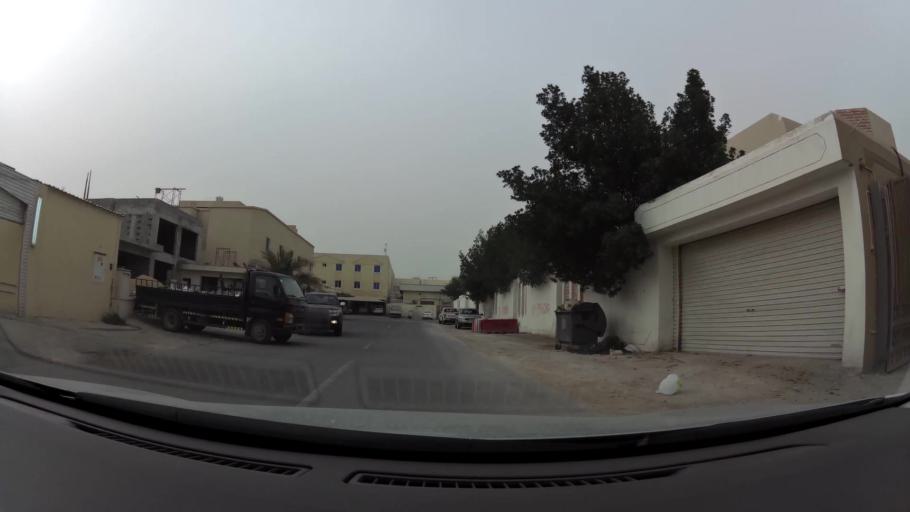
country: QA
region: Baladiyat ad Dawhah
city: Doha
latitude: 25.2594
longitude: 51.4924
